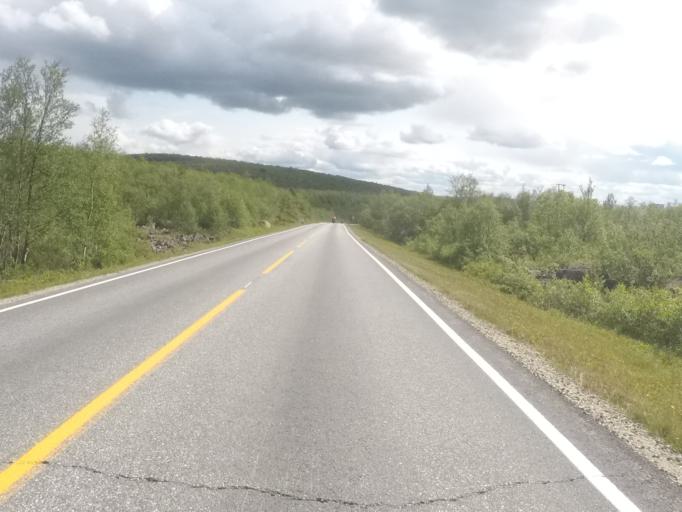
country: NO
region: Finnmark Fylke
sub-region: Karasjok
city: Karasjohka
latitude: 69.5114
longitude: 25.4668
